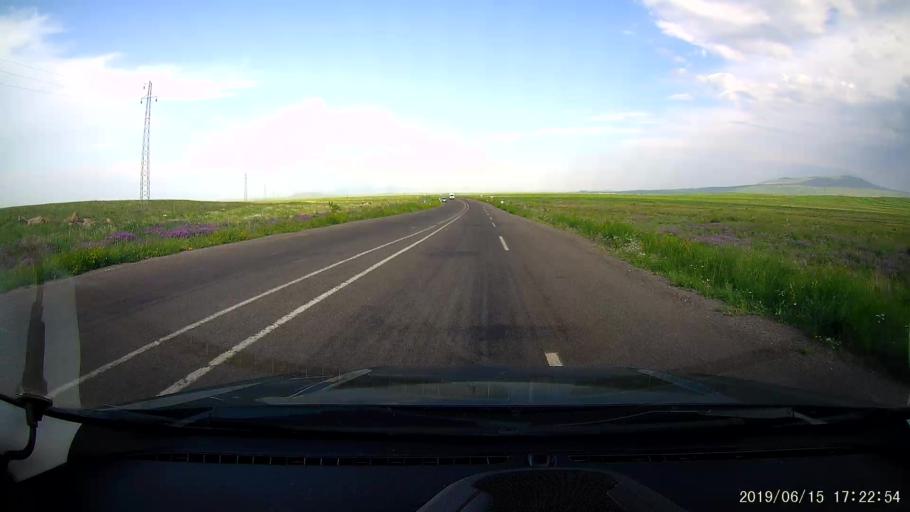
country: TR
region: Kars
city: Basgedikler
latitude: 40.6186
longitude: 43.3518
